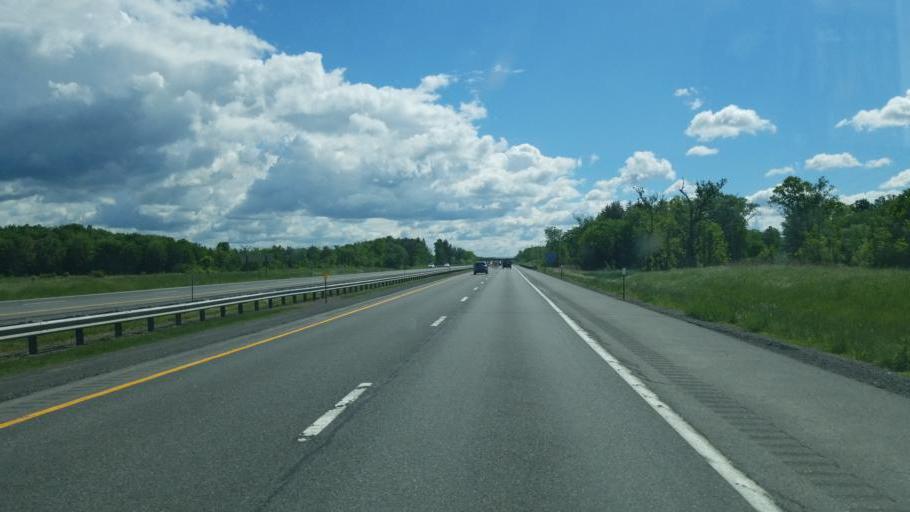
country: US
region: New York
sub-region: Oneida County
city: Vernon
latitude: 43.1327
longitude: -75.5117
